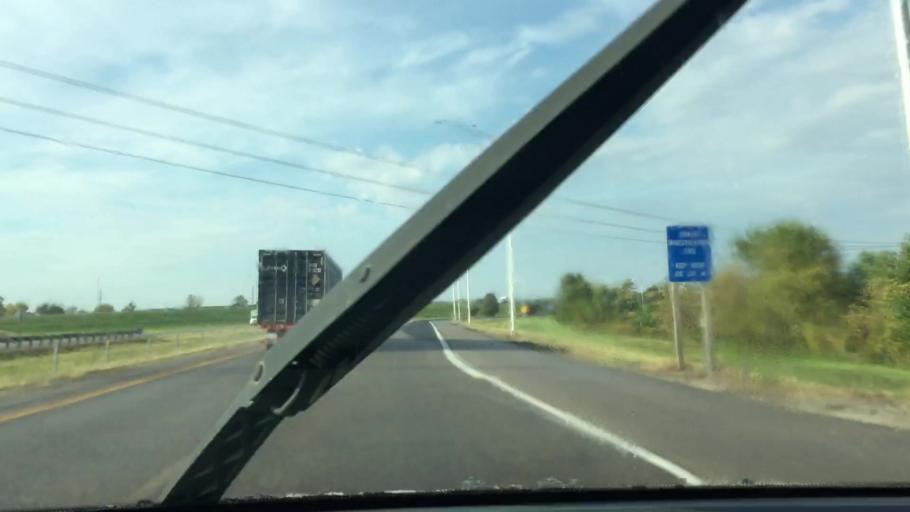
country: US
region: Illinois
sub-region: Whiteside County
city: Rock Falls
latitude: 41.7612
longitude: -89.6337
